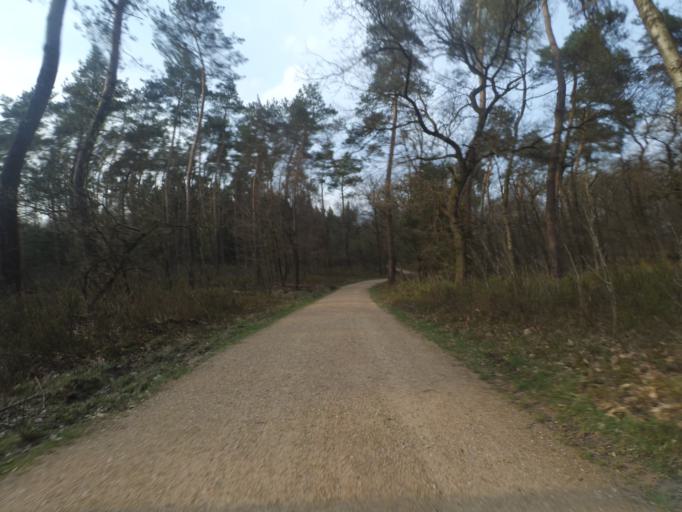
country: NL
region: Gelderland
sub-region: Gemeente Apeldoorn
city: Beekbergen
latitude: 52.1480
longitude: 5.8845
